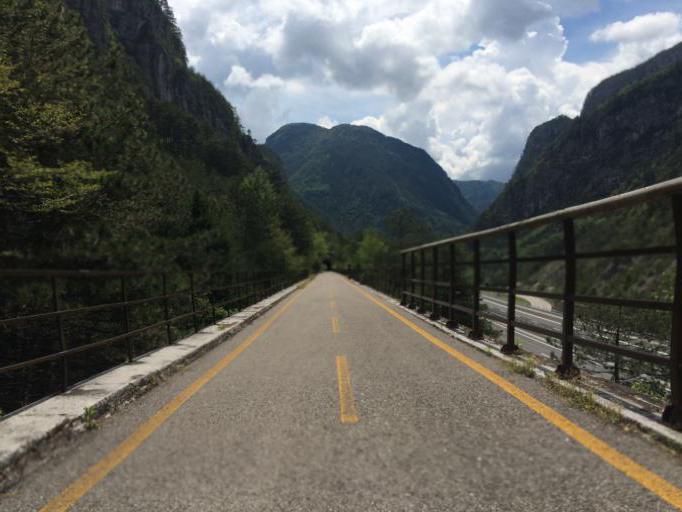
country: IT
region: Friuli Venezia Giulia
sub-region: Provincia di Udine
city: Dogna
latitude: 46.4327
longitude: 13.3149
